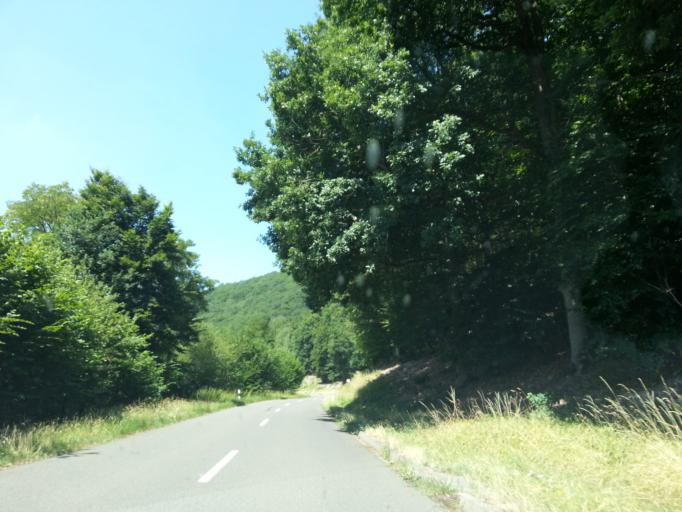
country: DE
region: Rheinland-Pfalz
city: Piesport
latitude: 49.8908
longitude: 6.9262
